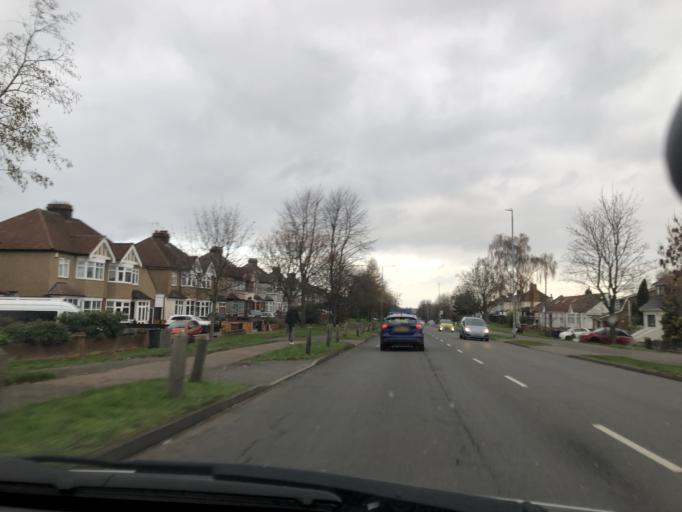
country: GB
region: England
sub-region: Kent
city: Dartford
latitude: 51.4423
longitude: 0.1953
